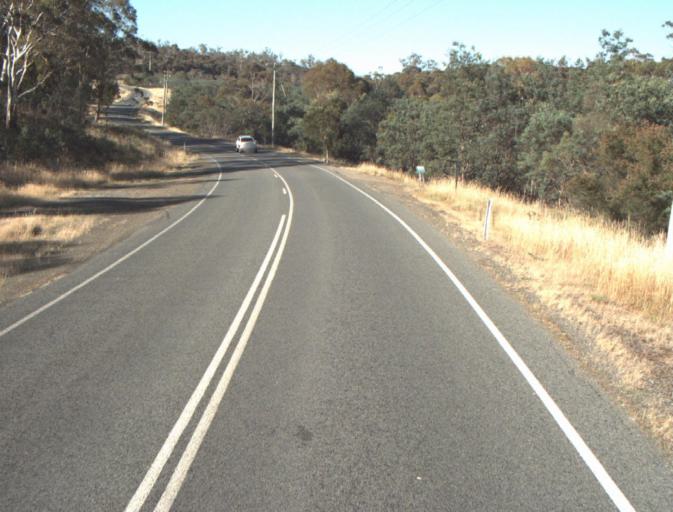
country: AU
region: Tasmania
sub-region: Launceston
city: Newstead
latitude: -41.4290
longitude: 147.2526
